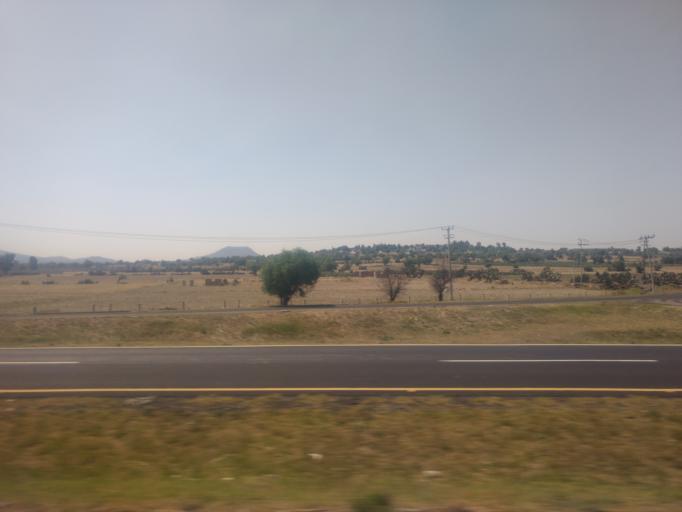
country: MX
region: Morelos
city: Nopaltepec
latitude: 19.7714
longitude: -98.7432
